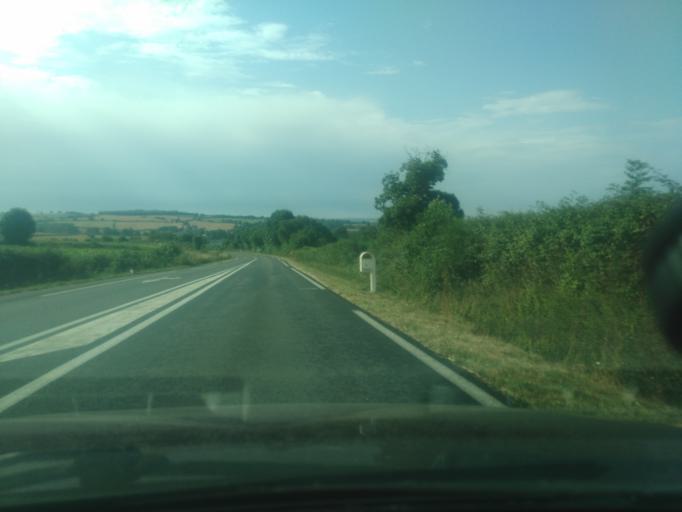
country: FR
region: Pays de la Loire
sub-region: Departement de la Vendee
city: Saint-Pierre-du-Chemin
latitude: 46.6493
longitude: -0.6601
